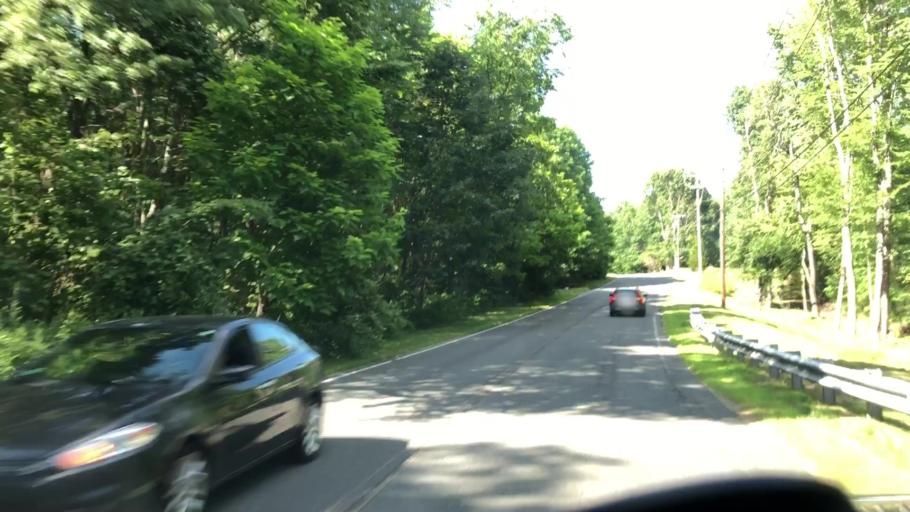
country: US
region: Massachusetts
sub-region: Hampshire County
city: Southampton
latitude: 42.2189
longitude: -72.6902
